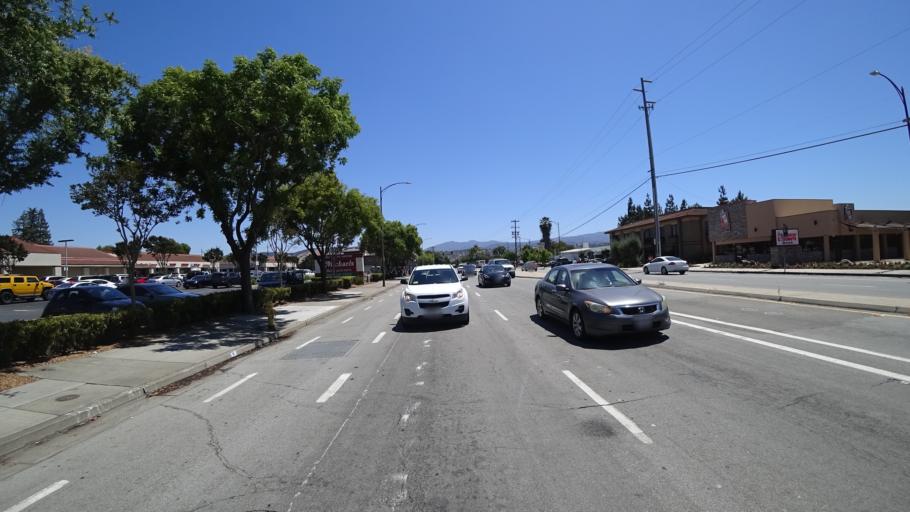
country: US
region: California
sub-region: Santa Clara County
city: Seven Trees
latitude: 37.2529
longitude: -121.8308
